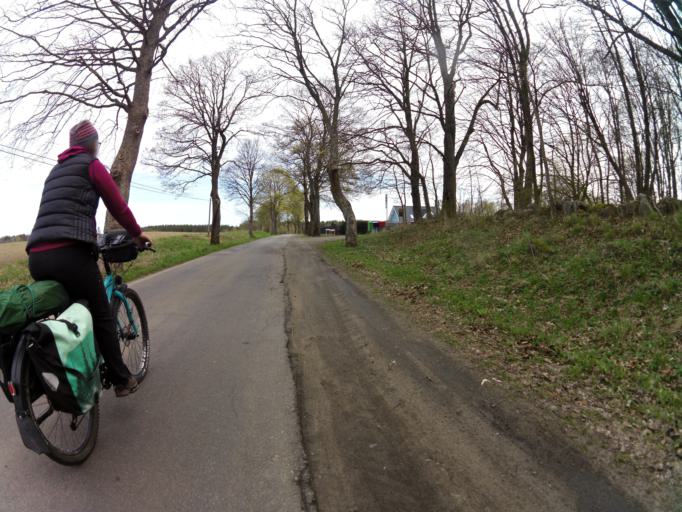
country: PL
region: West Pomeranian Voivodeship
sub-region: Powiat szczecinecki
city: Borne Sulinowo
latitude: 53.7136
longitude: 16.5407
